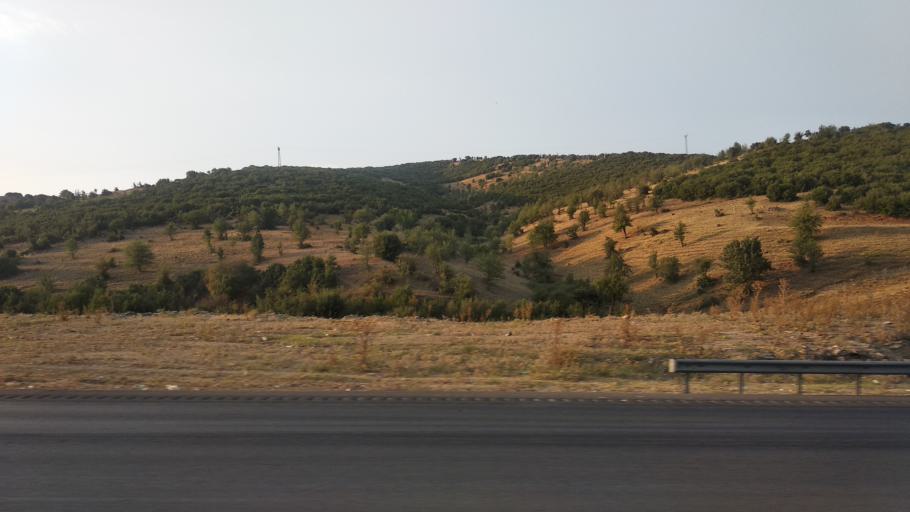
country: TR
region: Manisa
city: Menye
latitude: 38.5540
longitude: 28.4754
